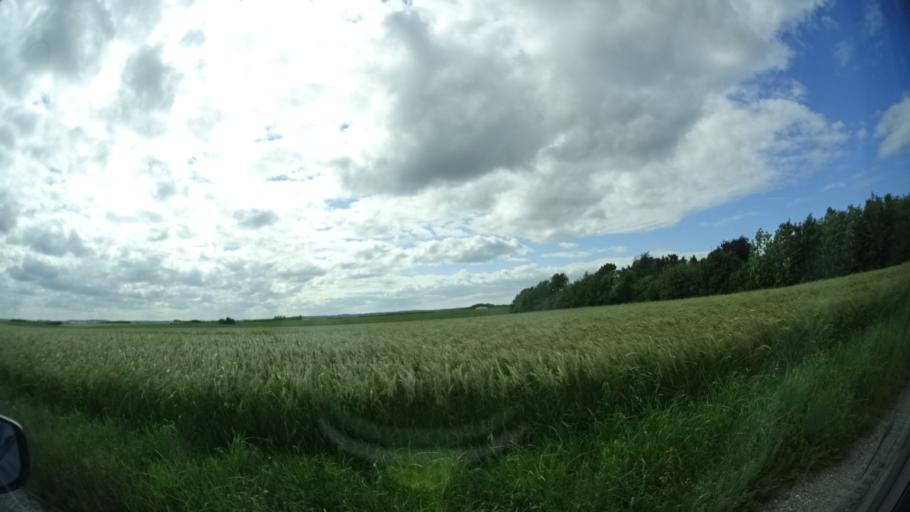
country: DK
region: Central Jutland
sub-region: Norddjurs Kommune
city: Grenaa
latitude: 56.4670
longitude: 10.7148
